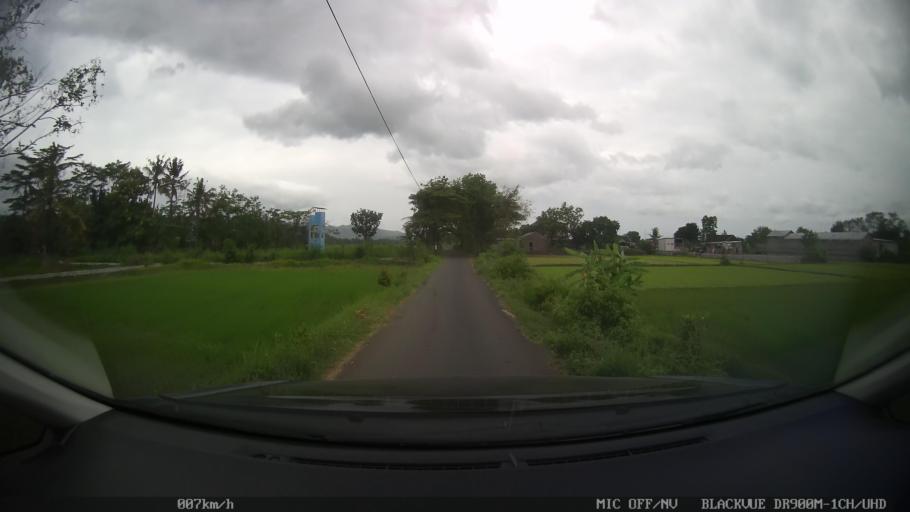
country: ID
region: Daerah Istimewa Yogyakarta
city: Sewon
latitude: -7.8558
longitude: 110.4159
